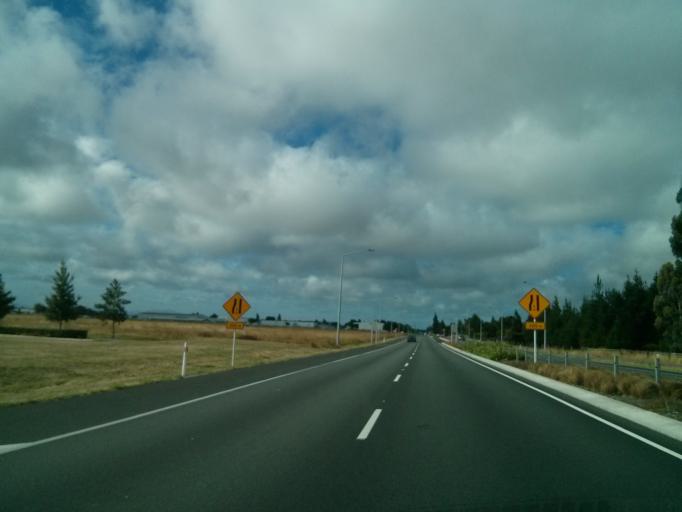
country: NZ
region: Canterbury
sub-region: Selwyn District
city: Prebbleton
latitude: -43.5018
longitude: 172.5449
